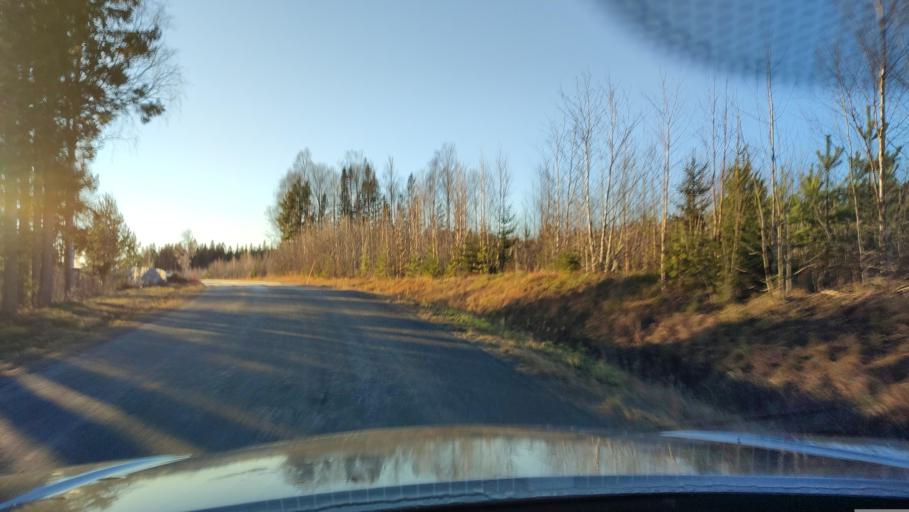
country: SE
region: Vaesterbotten
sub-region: Skelleftea Kommun
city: Viken
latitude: 64.7103
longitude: 20.9057
